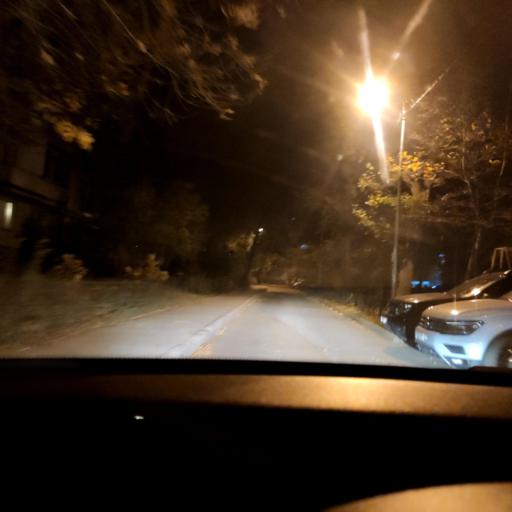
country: RU
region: Samara
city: Samara
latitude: 53.2343
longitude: 50.2127
